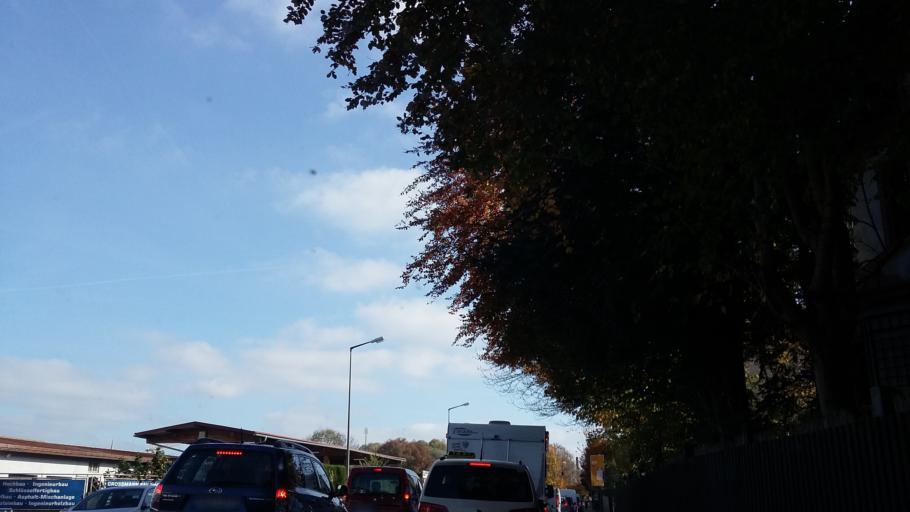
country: DE
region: Bavaria
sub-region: Upper Bavaria
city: Rosenheim
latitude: 47.8527
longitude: 12.1036
